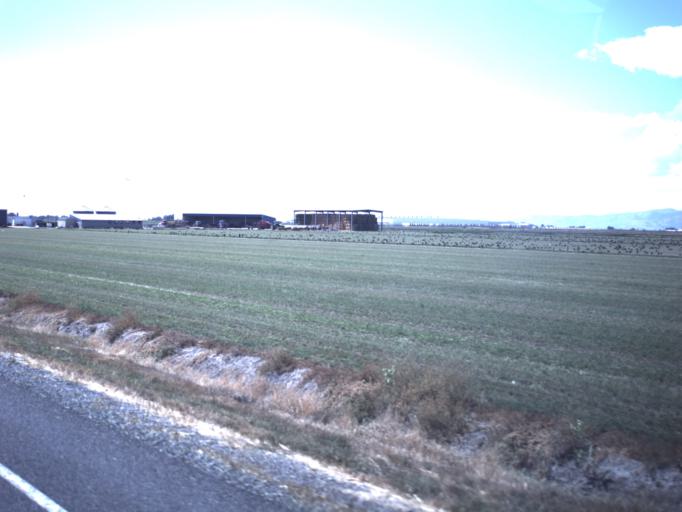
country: US
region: Utah
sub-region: Box Elder County
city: Honeyville
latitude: 41.5729
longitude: -112.1297
